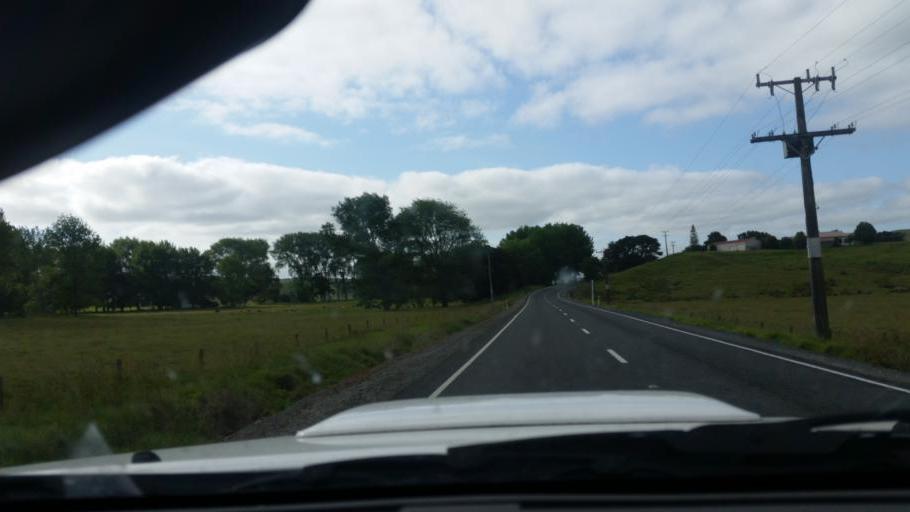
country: NZ
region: Northland
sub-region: Kaipara District
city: Dargaville
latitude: -35.8424
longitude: 173.8434
